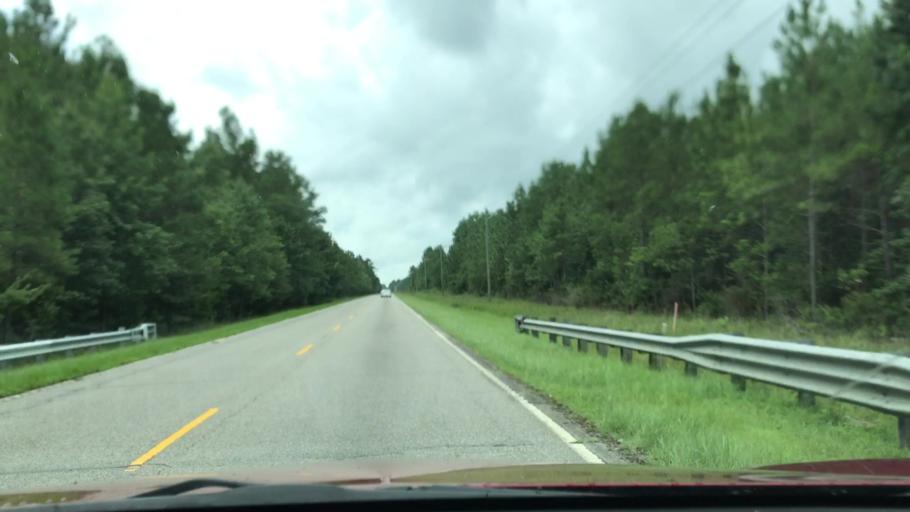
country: US
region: South Carolina
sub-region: Georgetown County
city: Murrells Inlet
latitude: 33.5819
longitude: -79.2071
